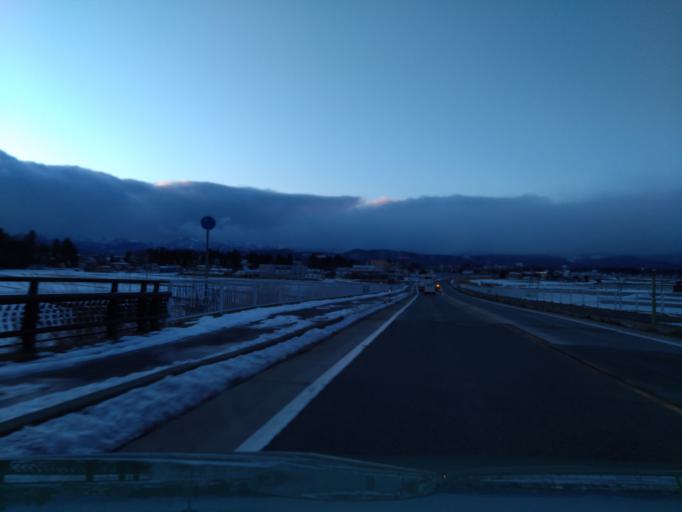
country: JP
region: Iwate
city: Shizukuishi
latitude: 39.6913
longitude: 140.9861
